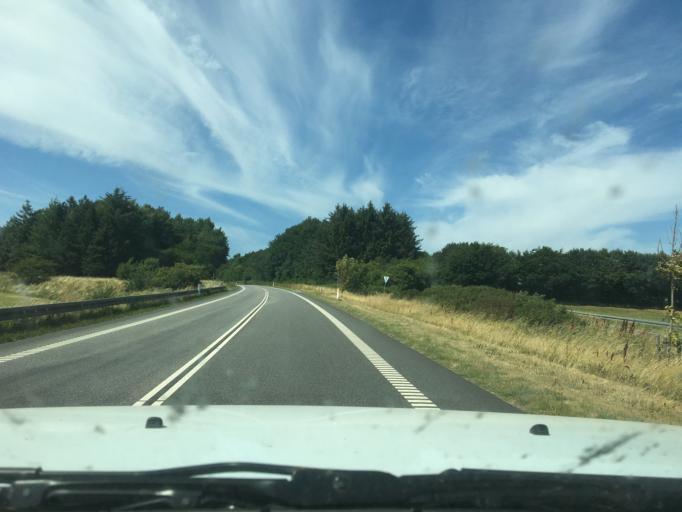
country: DK
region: Central Jutland
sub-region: Viborg Kommune
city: Viborg
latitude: 56.5439
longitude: 9.4019
